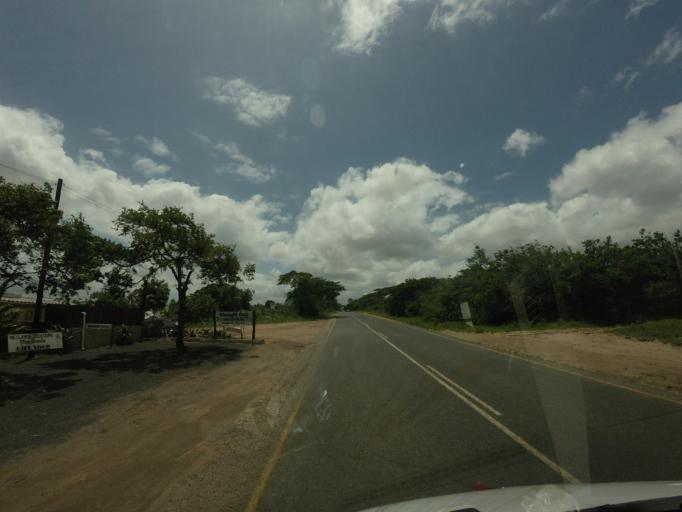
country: ZA
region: KwaZulu-Natal
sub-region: uMkhanyakude District Municipality
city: Mtubatuba
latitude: -28.3849
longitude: 32.3498
